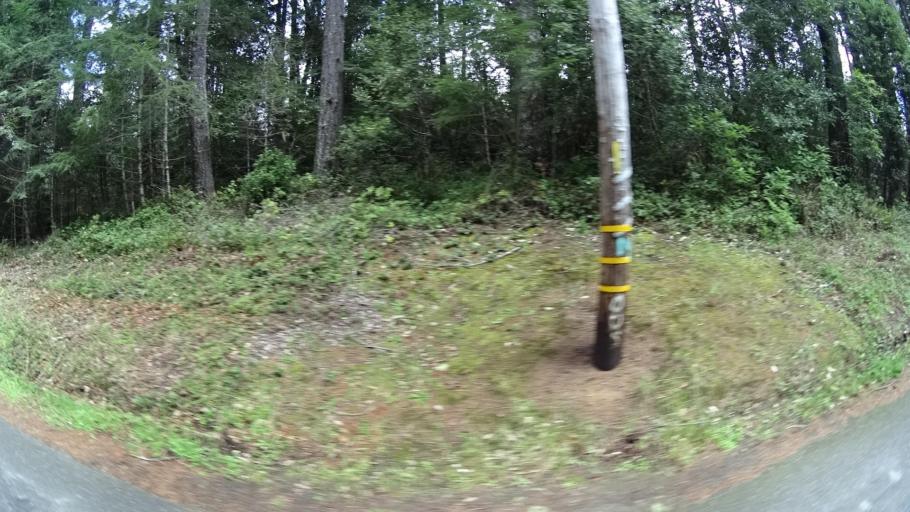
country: US
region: California
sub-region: Humboldt County
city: Blue Lake
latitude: 40.8030
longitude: -123.9853
